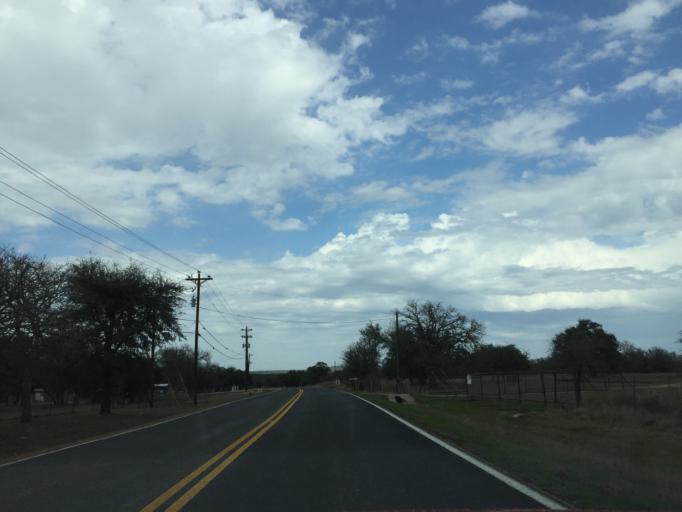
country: US
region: Texas
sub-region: Burnet County
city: Bertram
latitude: 30.7033
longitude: -97.9294
